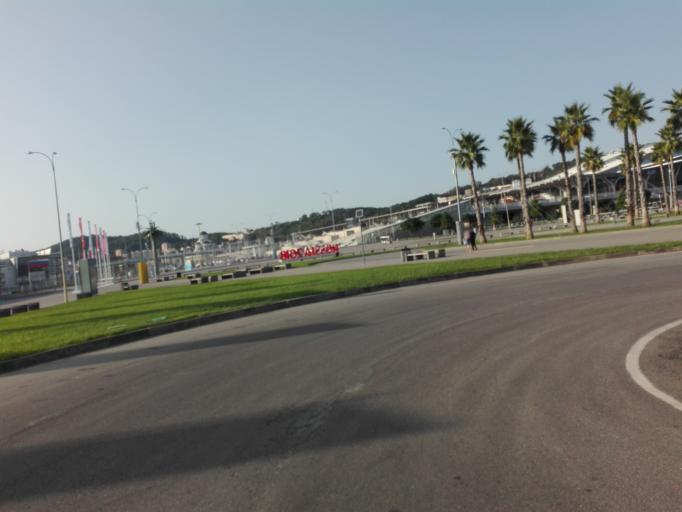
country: RU
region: Krasnodarskiy
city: Adler
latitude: 43.4090
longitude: 39.9730
